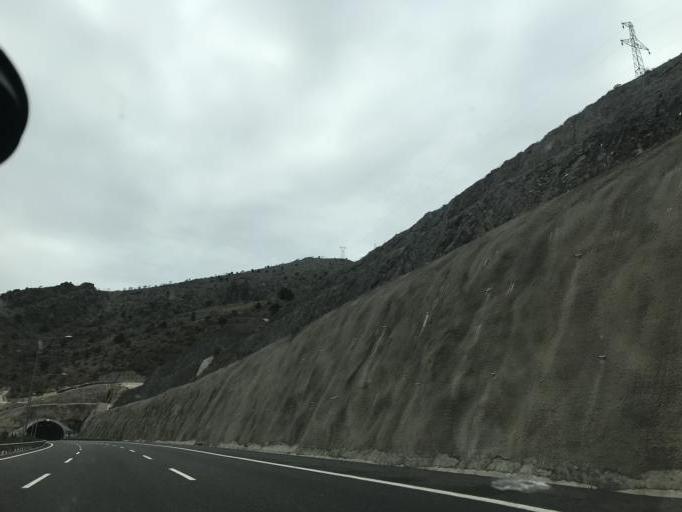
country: TR
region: Nigde
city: Ciftehan
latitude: 37.5475
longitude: 34.7836
